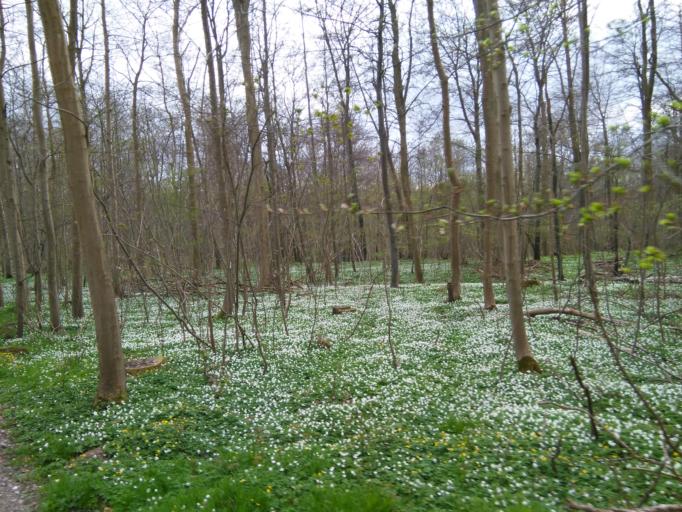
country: DK
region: Central Jutland
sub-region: Arhus Kommune
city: Beder
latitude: 56.0869
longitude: 10.2034
